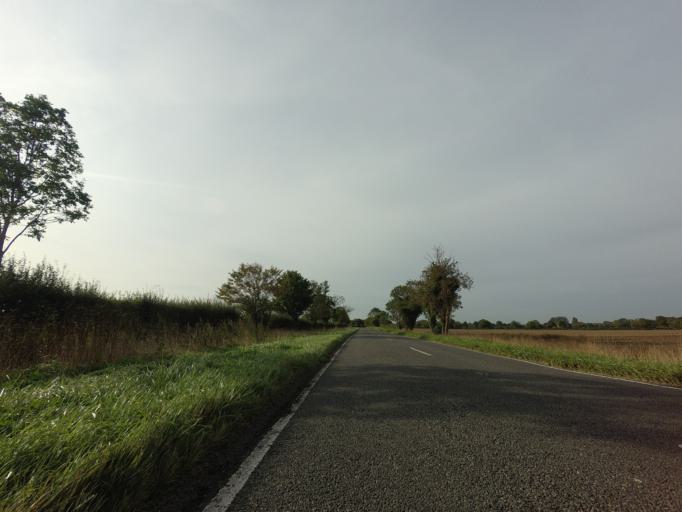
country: GB
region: England
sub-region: Cambridgeshire
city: Harston
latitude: 52.0998
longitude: 0.0833
